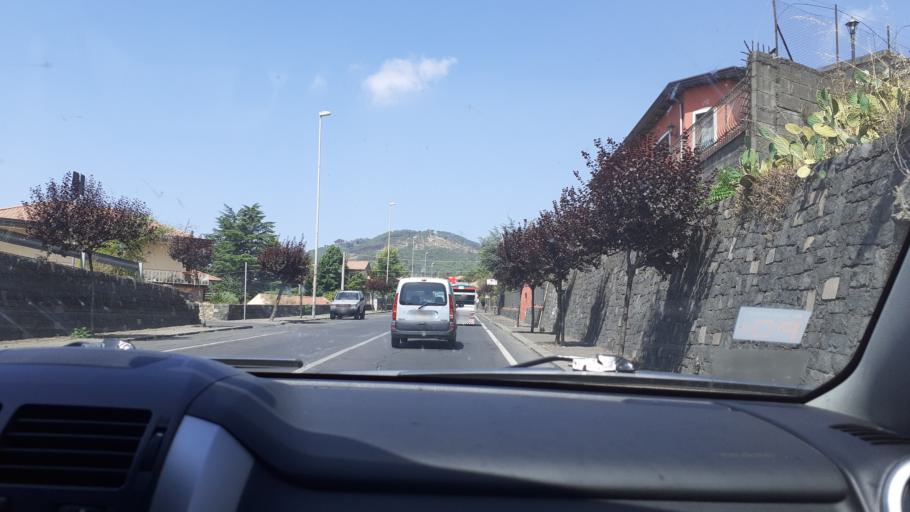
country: IT
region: Sicily
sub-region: Catania
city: Nicolosi
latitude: 37.6165
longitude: 15.0323
